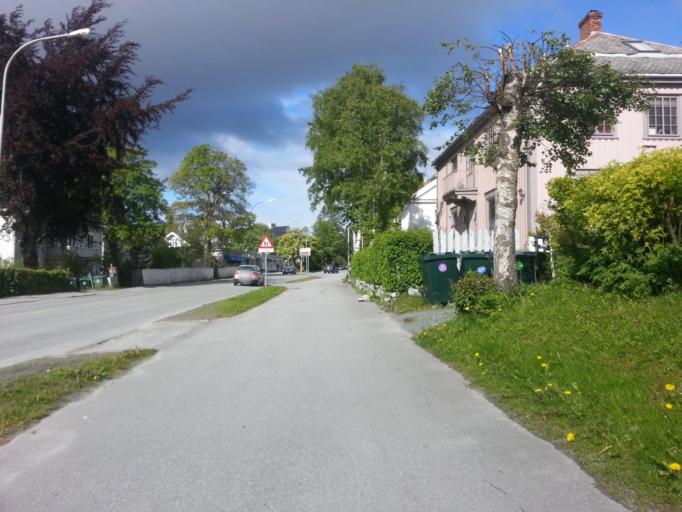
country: NO
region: Sor-Trondelag
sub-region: Trondheim
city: Trondheim
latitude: 63.4216
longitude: 10.4108
